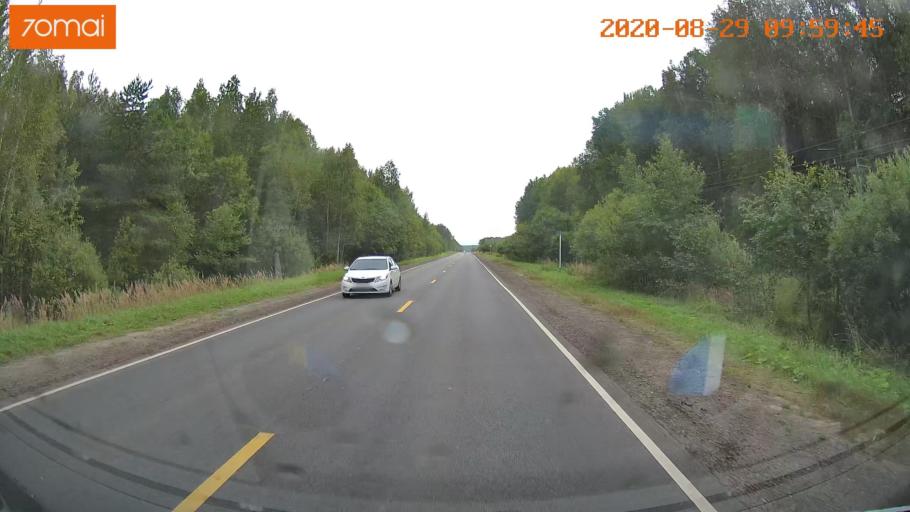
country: RU
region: Ivanovo
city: Zarechnyy
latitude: 57.4106
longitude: 42.3747
